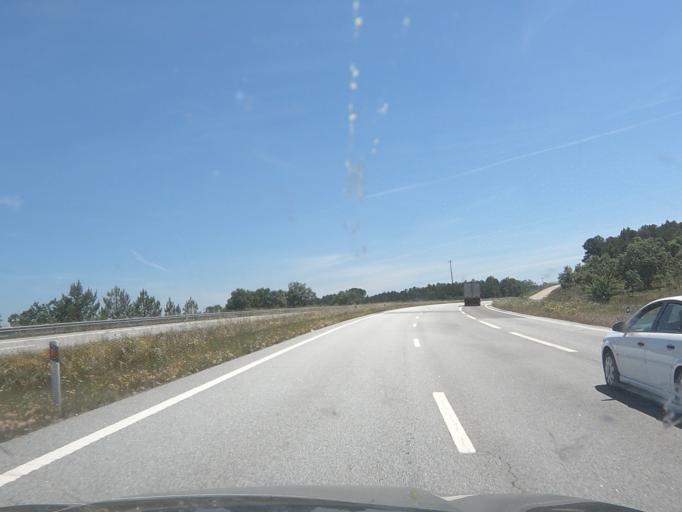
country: PT
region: Guarda
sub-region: Pinhel
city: Pinhel
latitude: 40.6105
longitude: -7.0071
